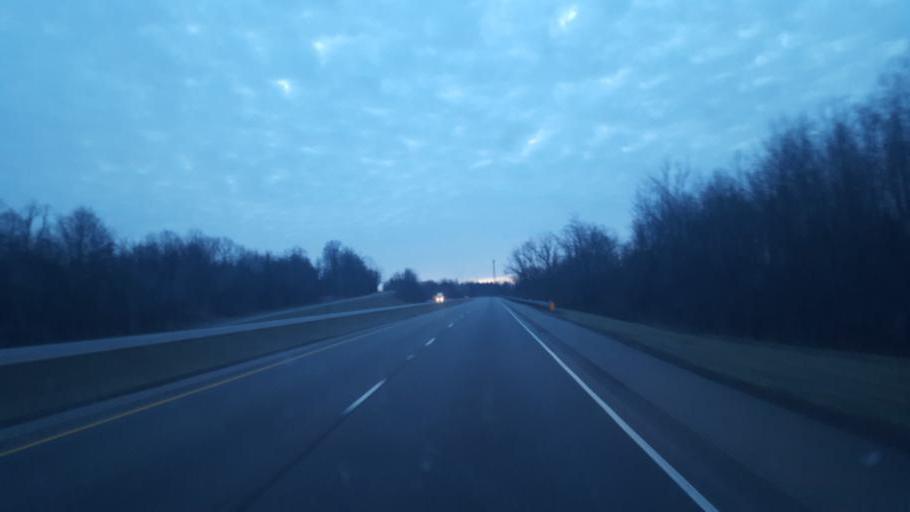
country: US
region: Ohio
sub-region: Jackson County
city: Oak Hill
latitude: 38.9721
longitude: -82.5095
